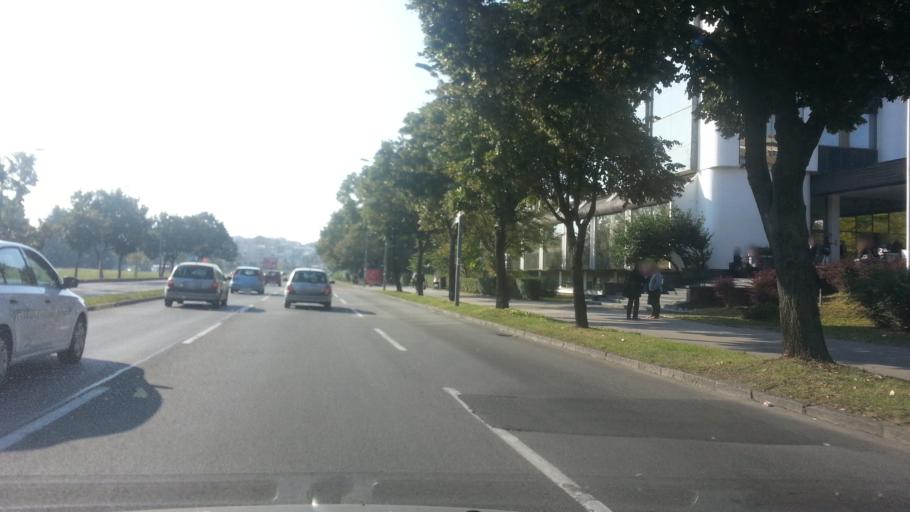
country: RS
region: Central Serbia
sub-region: Belgrade
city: Novi Beograd
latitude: 44.8280
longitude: 20.4195
